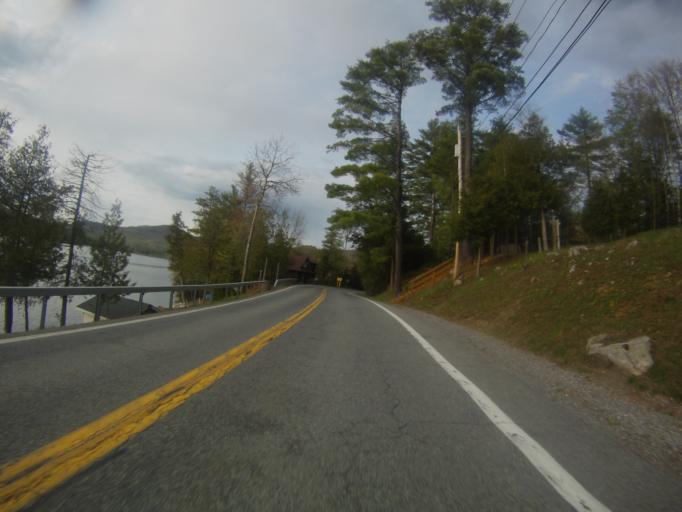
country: US
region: New York
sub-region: Warren County
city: Warrensburg
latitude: 43.7280
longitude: -73.6790
